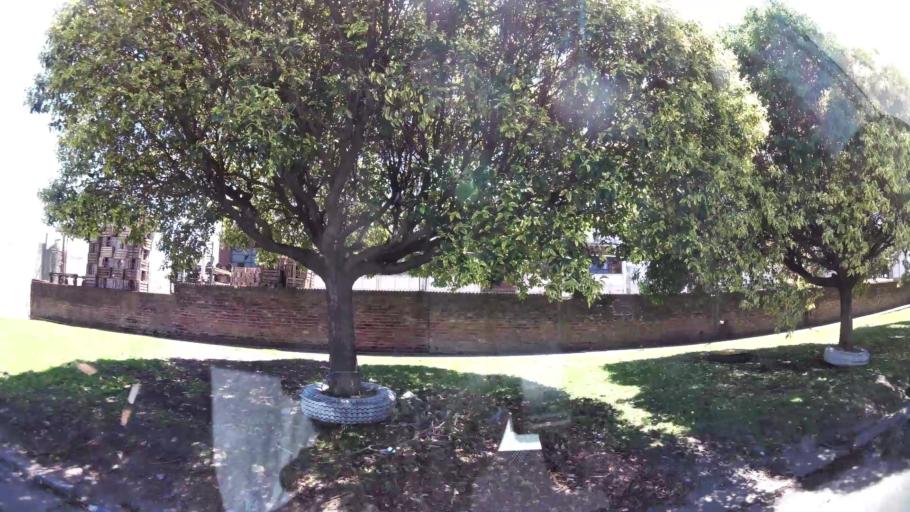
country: AR
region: Buenos Aires
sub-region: Partido de Quilmes
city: Quilmes
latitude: -34.7334
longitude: -58.2796
